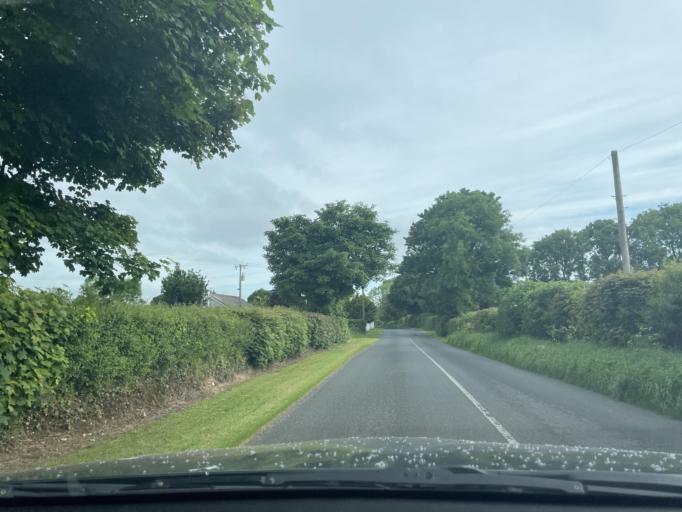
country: IE
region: Leinster
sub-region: County Carlow
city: Bagenalstown
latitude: 52.6631
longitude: -6.9630
